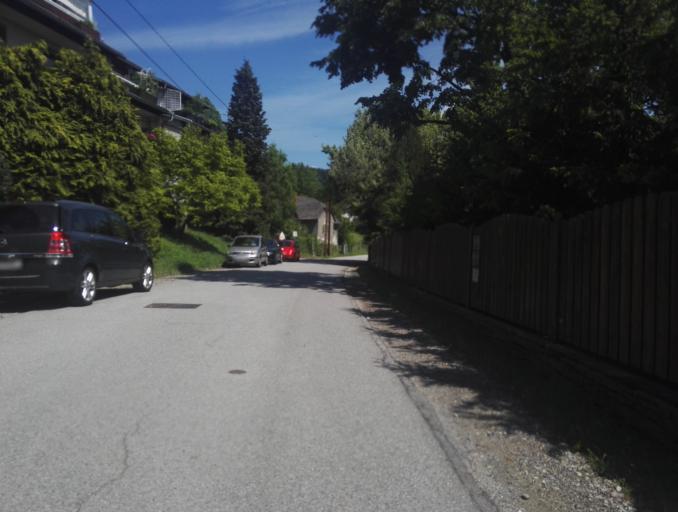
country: AT
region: Styria
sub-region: Graz Stadt
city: Goesting
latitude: 47.1028
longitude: 15.3934
